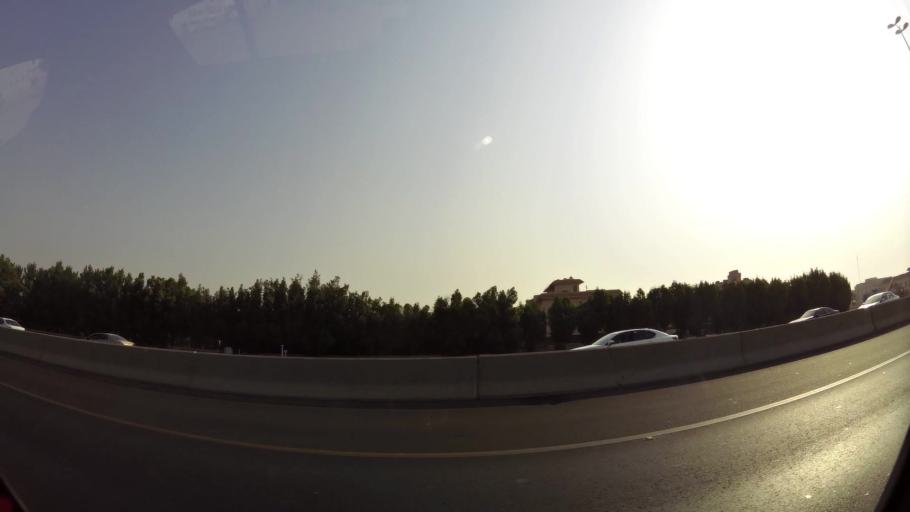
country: KW
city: Al Funaytis
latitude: 29.2292
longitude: 48.0980
